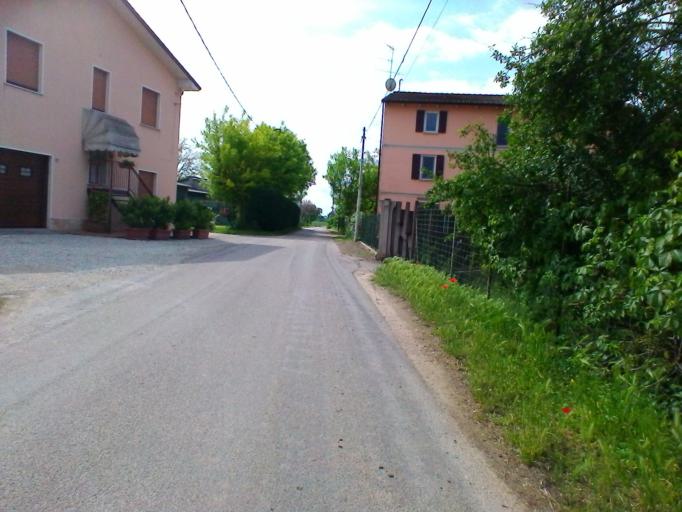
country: IT
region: Lombardy
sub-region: Provincia di Mantova
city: San Biagio
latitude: 45.1239
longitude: 10.8251
